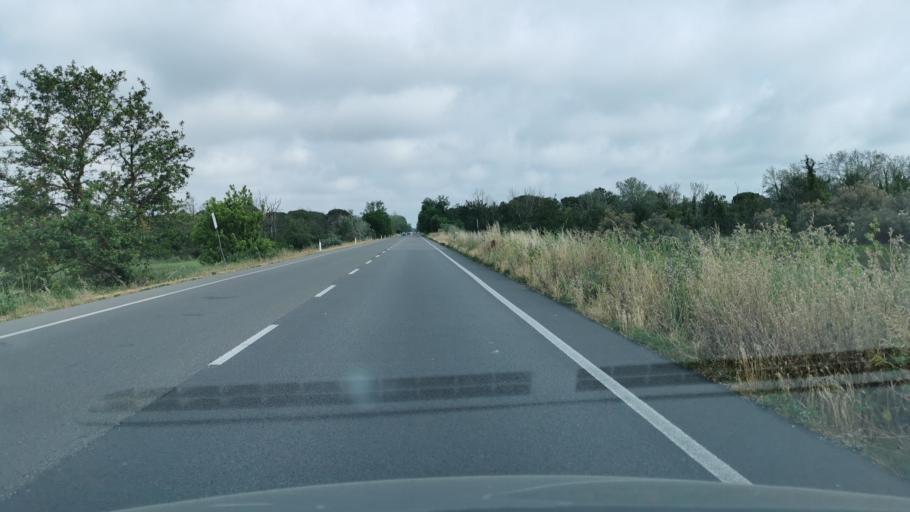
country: IT
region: Emilia-Romagna
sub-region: Provincia di Ravenna
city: Marina Romea
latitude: 44.5873
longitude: 12.2524
